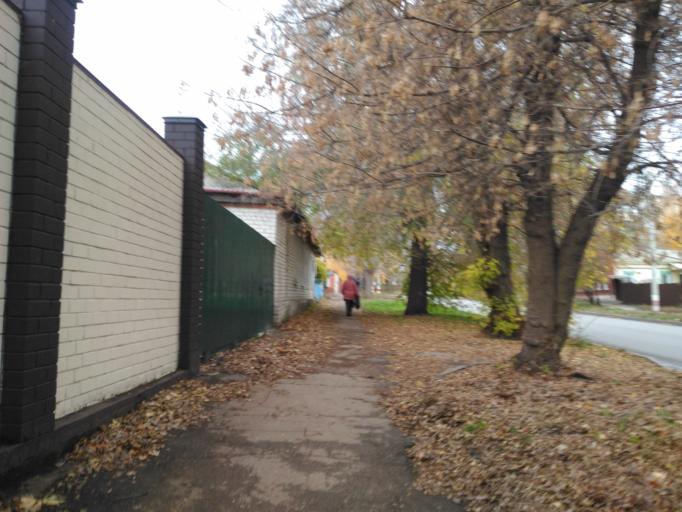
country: RU
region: Ulyanovsk
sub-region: Ulyanovskiy Rayon
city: Ulyanovsk
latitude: 54.3382
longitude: 48.3945
